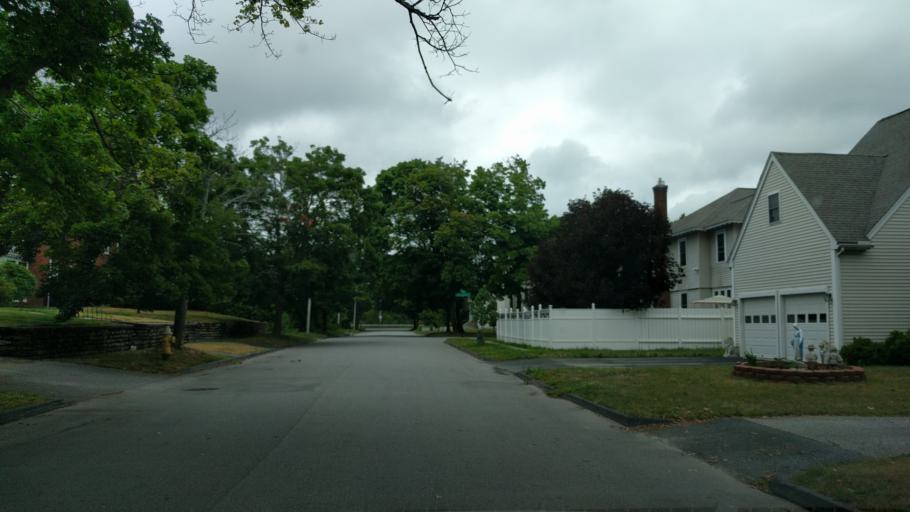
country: US
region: Massachusetts
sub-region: Worcester County
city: Worcester
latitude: 42.2886
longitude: -71.7895
